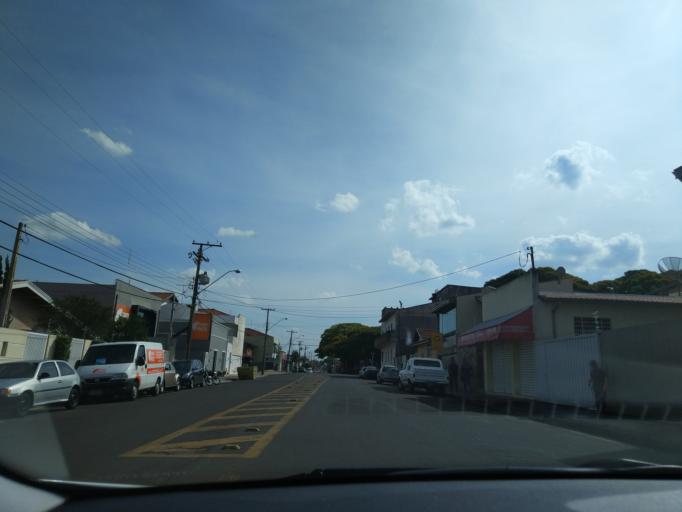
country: BR
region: Sao Paulo
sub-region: Botucatu
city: Botucatu
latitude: -22.8689
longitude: -48.4428
